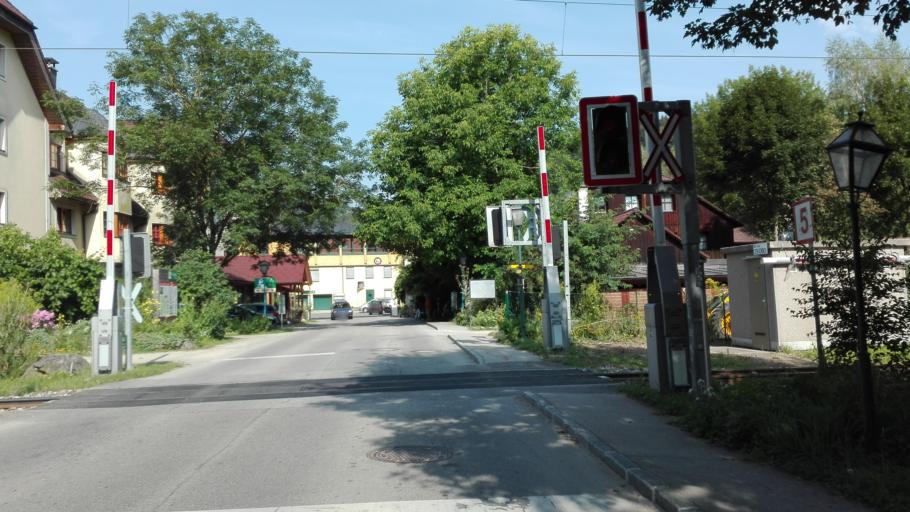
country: AT
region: Lower Austria
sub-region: Politischer Bezirk Sankt Polten
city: Kirchberg an der Pielach
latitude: 48.0398
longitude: 15.4513
